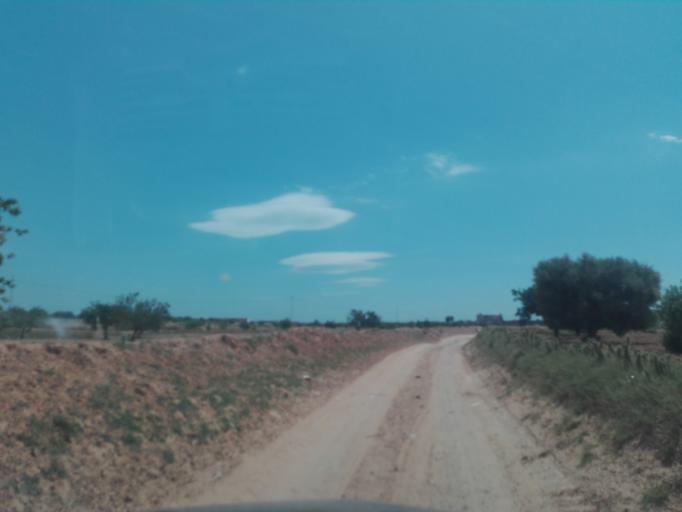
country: TN
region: Safaqis
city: Sfax
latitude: 34.6509
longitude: 10.5944
